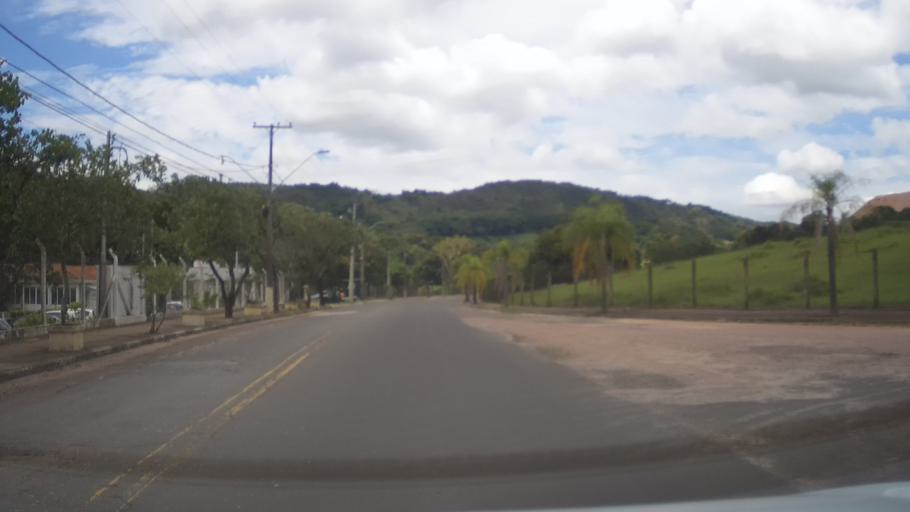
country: BR
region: Sao Paulo
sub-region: Valinhos
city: Valinhos
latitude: -22.9900
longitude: -46.9778
